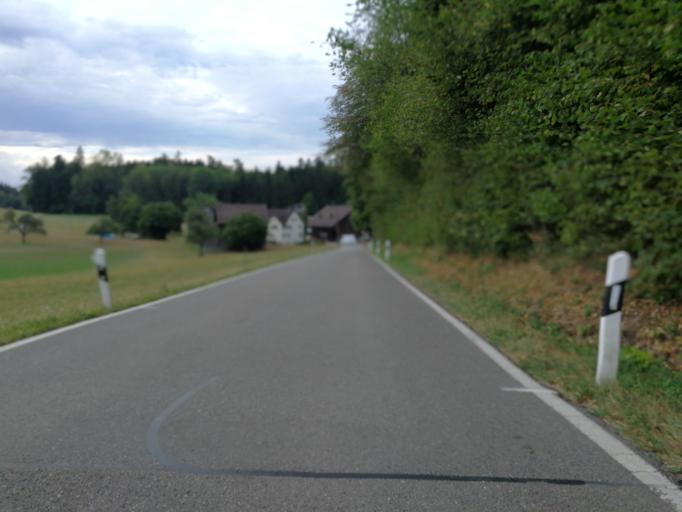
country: CH
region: Zurich
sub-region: Bezirk Hinwil
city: Gossau
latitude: 47.3246
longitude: 8.7631
